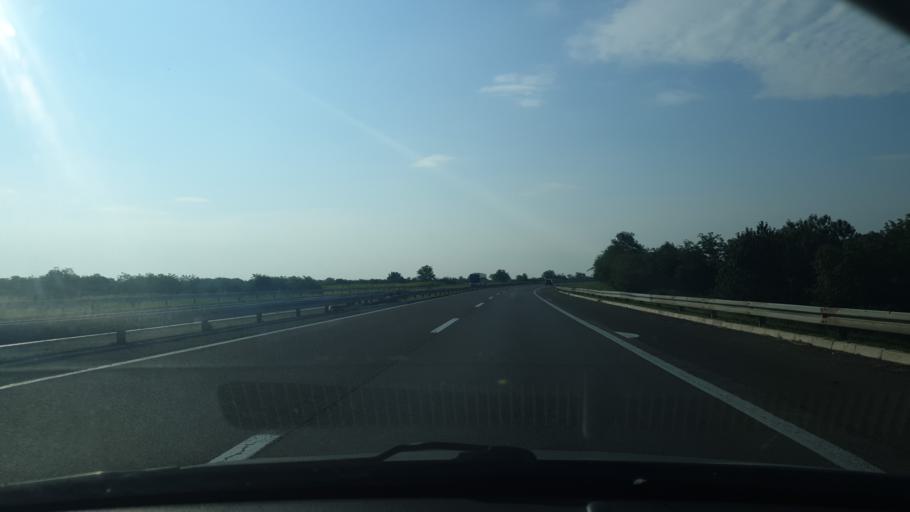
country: RS
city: Lugavcina
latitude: 44.5392
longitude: 20.9954
